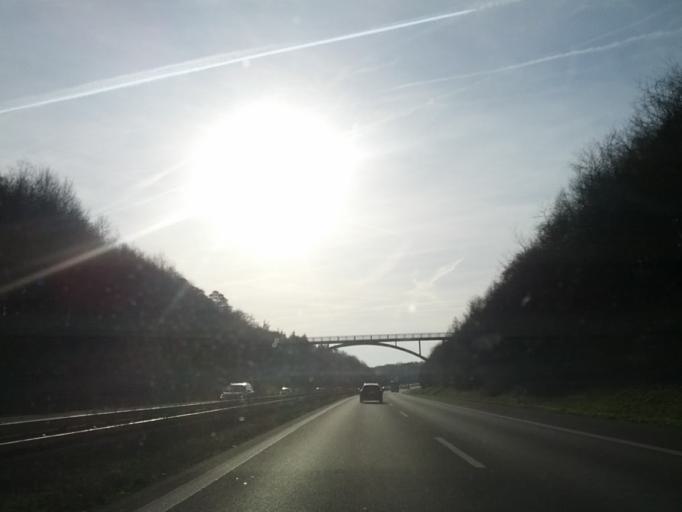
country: DE
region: Bavaria
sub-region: Regierungsbezirk Unterfranken
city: Unterpleichfeld
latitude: 49.8954
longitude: 10.0013
